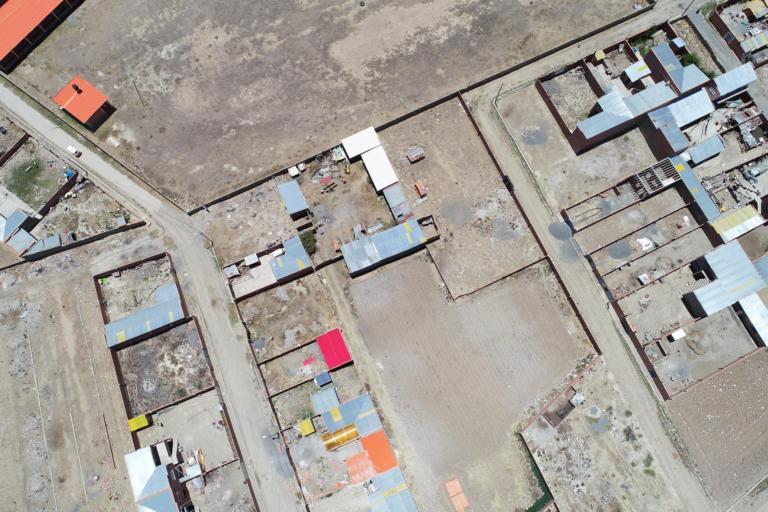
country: BO
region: La Paz
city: Achacachi
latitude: -16.0483
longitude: -68.6893
